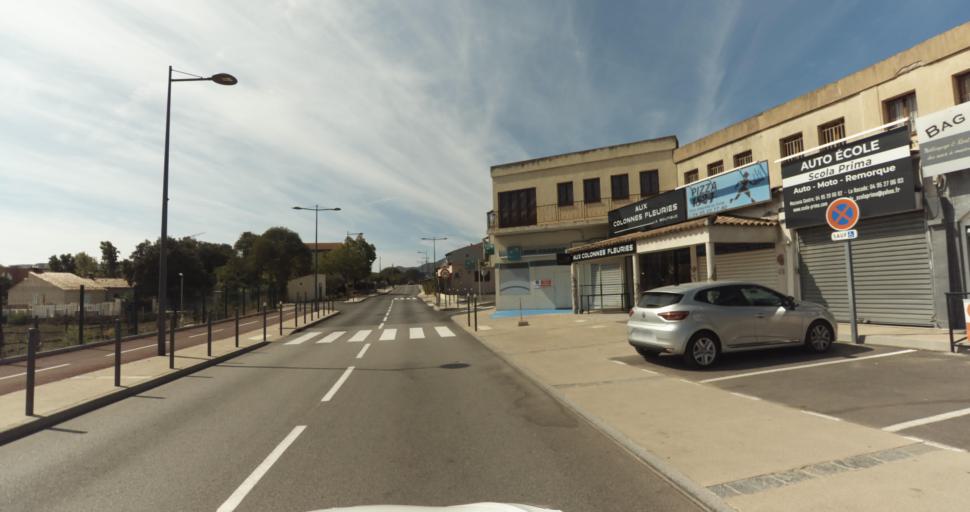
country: FR
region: Corsica
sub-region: Departement de la Corse-du-Sud
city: Afa
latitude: 41.9522
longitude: 8.7796
